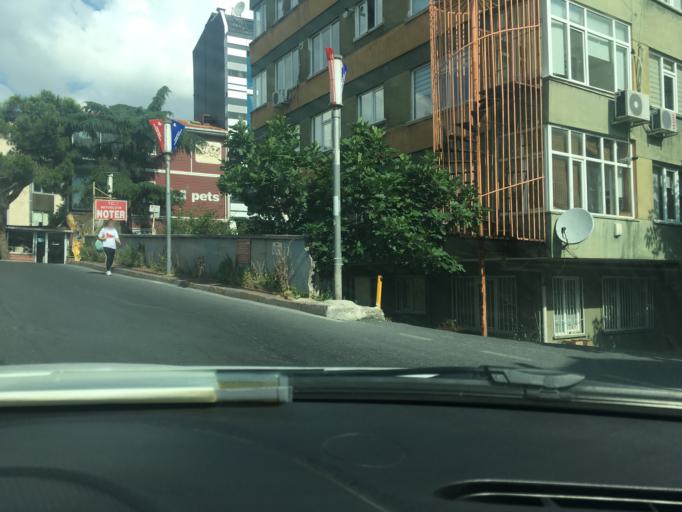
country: TR
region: Istanbul
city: Sisli
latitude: 41.0694
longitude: 29.0026
